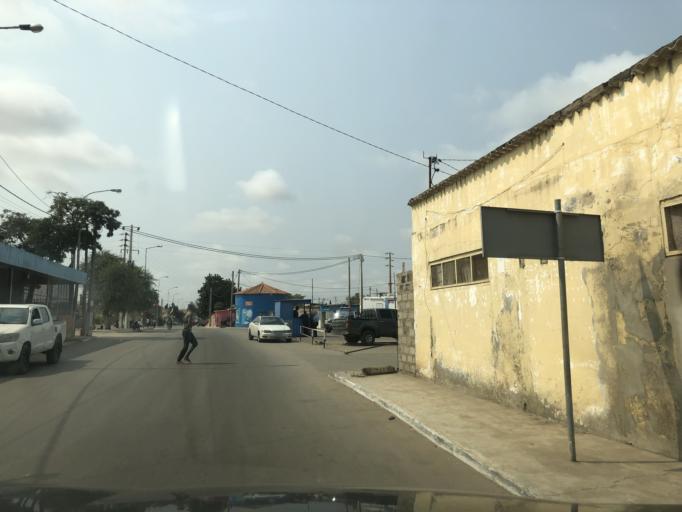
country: AO
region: Luanda
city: Luanda
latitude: -8.9104
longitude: 13.1590
